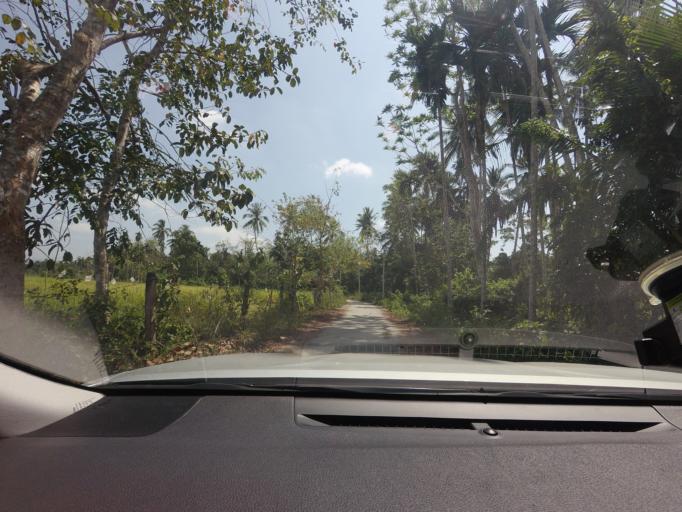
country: TH
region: Narathiwat
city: Rueso
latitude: 6.3802
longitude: 101.4986
